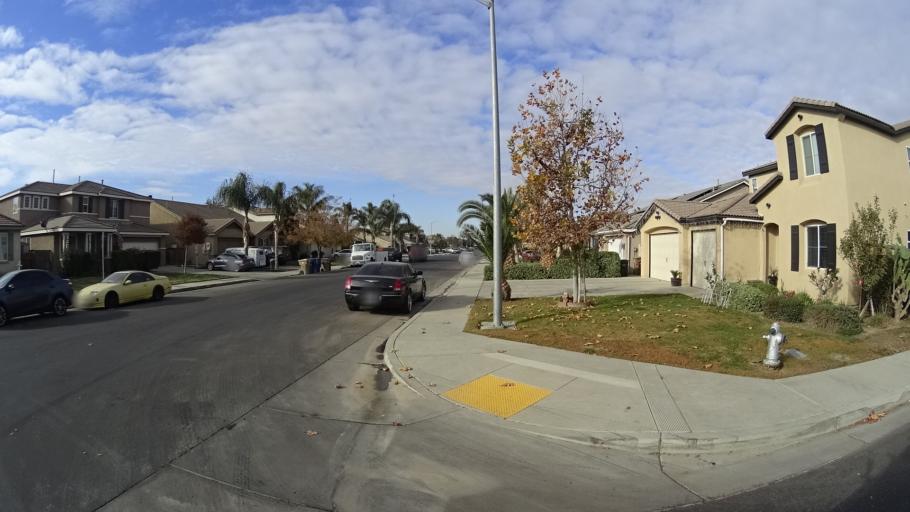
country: US
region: California
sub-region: Kern County
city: Rosedale
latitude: 35.2977
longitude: -119.1336
